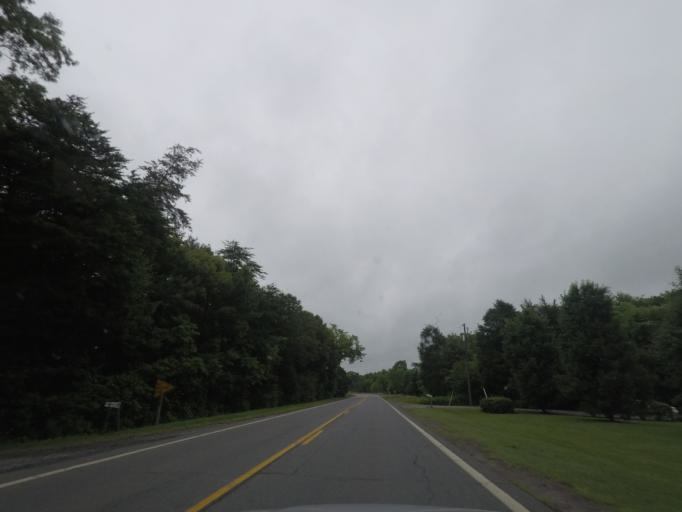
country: US
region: Virginia
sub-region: Fluvanna County
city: Weber City
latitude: 37.6960
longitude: -78.3193
